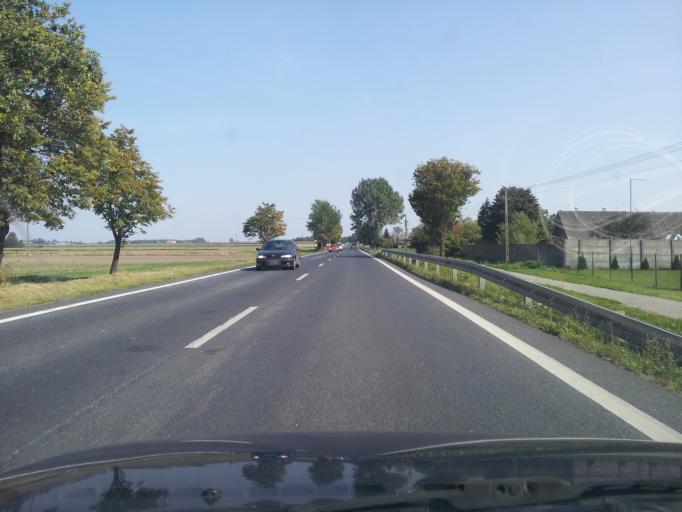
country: PL
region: Greater Poland Voivodeship
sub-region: Powiat gnieznienski
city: Lubowo
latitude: 52.5098
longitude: 17.4068
